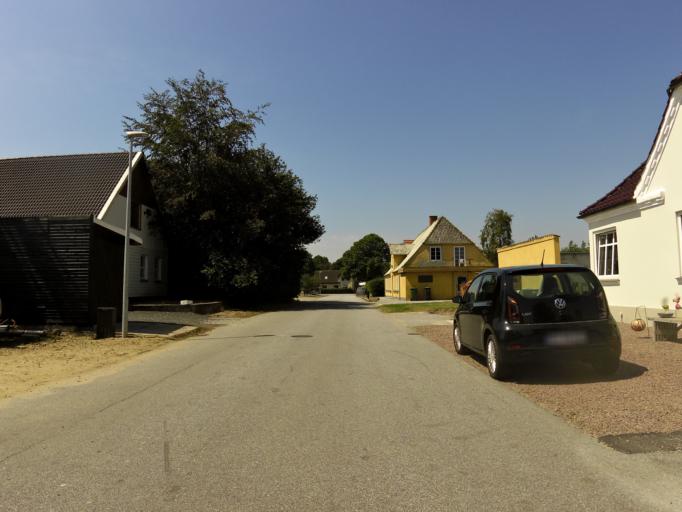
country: DK
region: South Denmark
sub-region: Haderslev Kommune
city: Vojens
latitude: 55.1583
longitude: 9.2538
